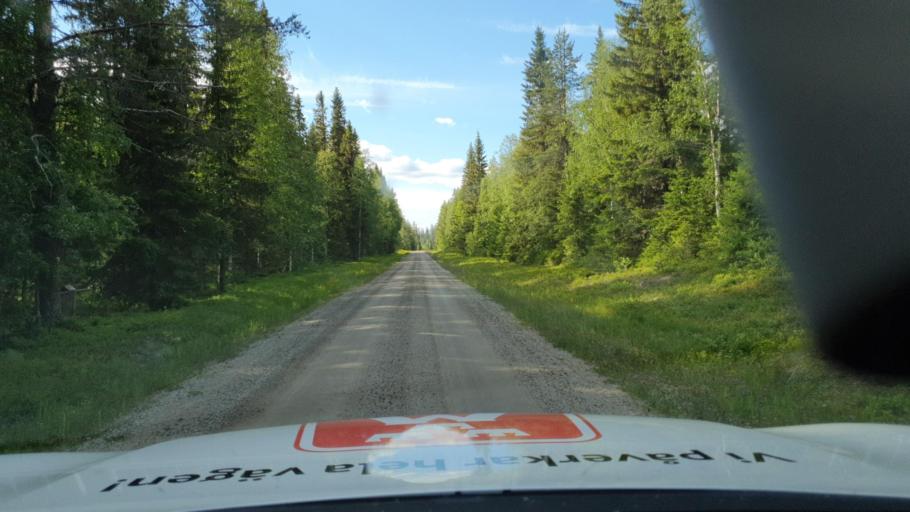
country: SE
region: Vaesterbotten
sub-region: Lycksele Kommun
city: Lycksele
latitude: 64.4613
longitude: 18.3039
